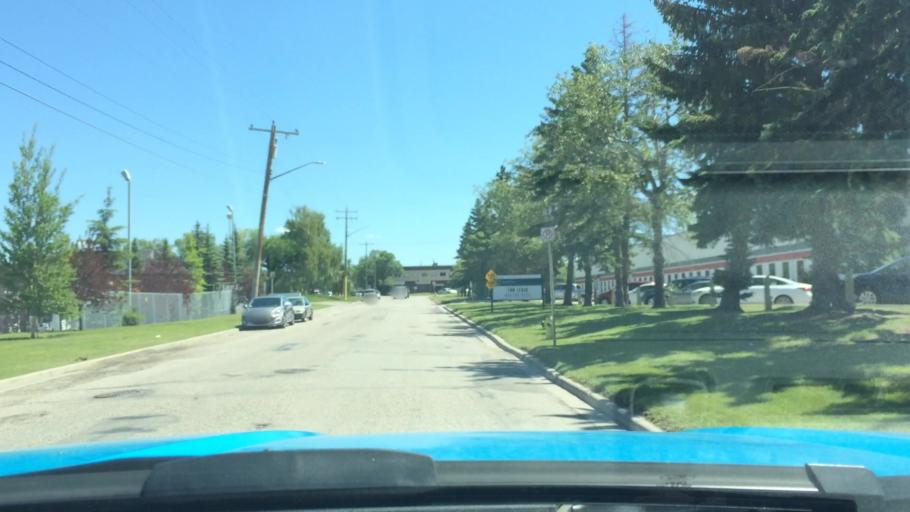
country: CA
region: Alberta
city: Calgary
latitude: 51.0899
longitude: -114.0076
